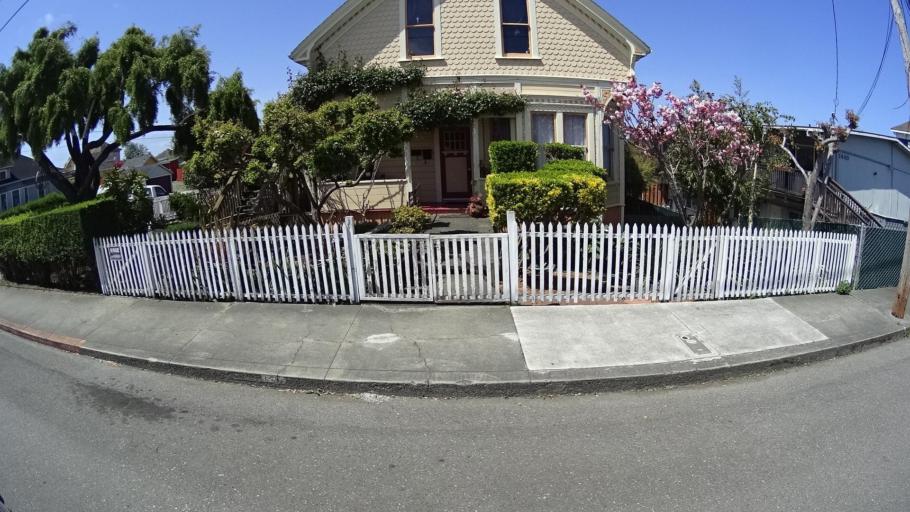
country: US
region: California
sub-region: Humboldt County
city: Eureka
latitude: 40.7931
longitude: -124.1719
